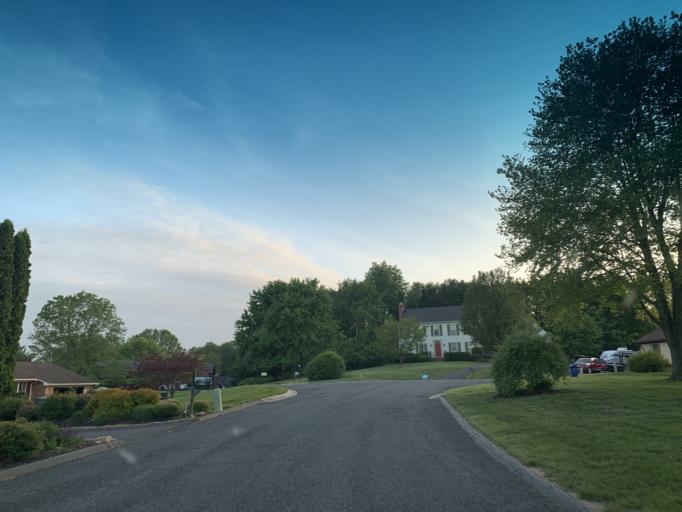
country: US
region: Maryland
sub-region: Harford County
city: South Bel Air
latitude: 39.5674
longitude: -76.2771
